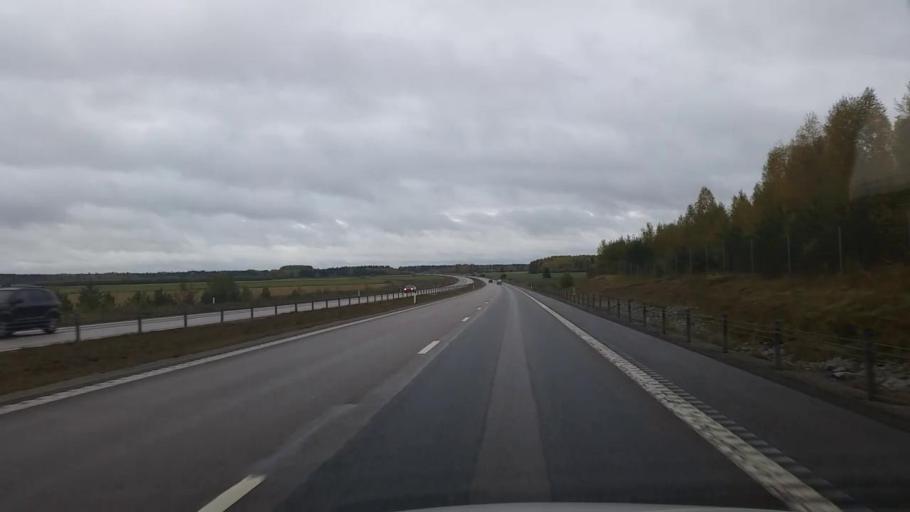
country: SE
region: Uppsala
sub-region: Osthammars Kommun
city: Bjorklinge
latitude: 60.1389
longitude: 17.5467
